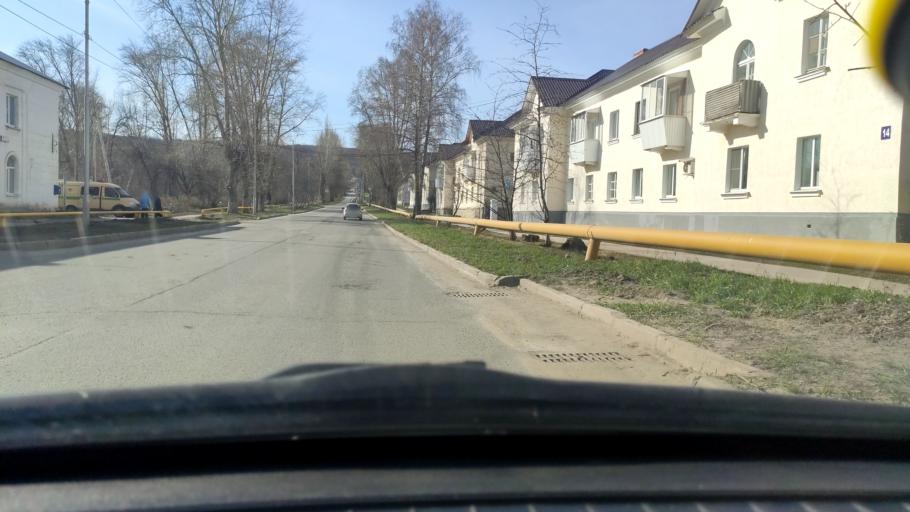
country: RU
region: Samara
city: Zhigulevsk
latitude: 53.4008
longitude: 49.4976
